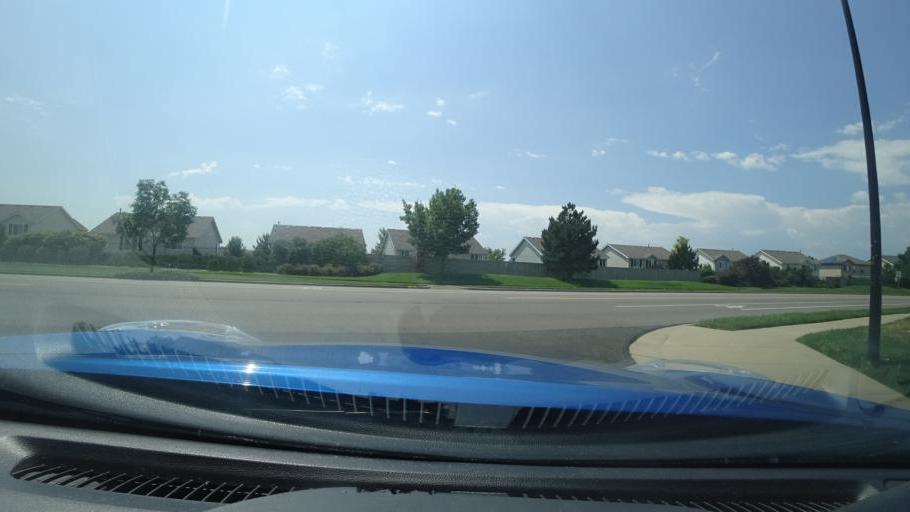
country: US
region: Colorado
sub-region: Adams County
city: Aurora
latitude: 39.6750
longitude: -104.7606
